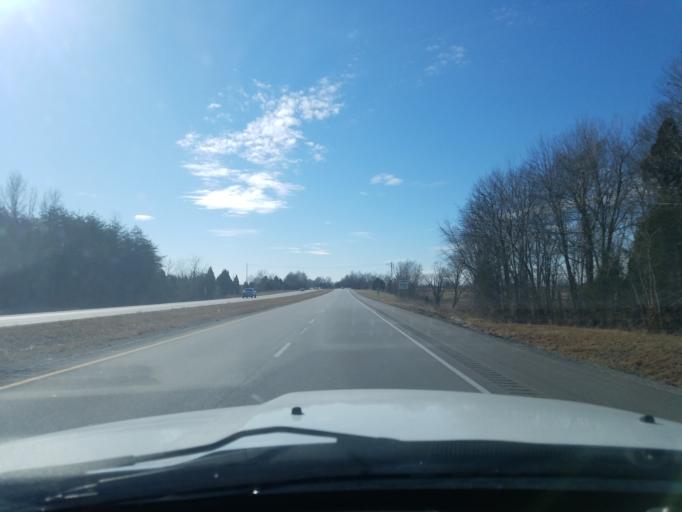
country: US
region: Kentucky
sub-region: Grayson County
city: Leitchfield
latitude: 37.5325
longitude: -86.1401
